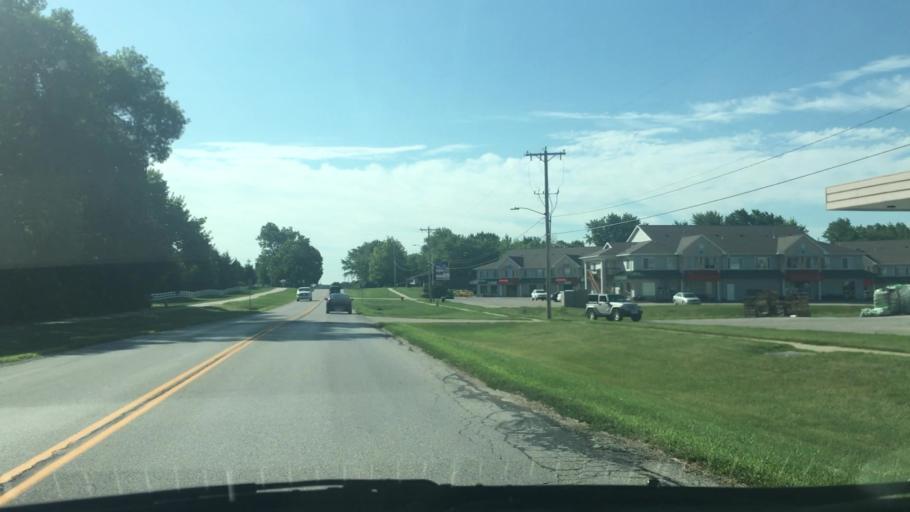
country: US
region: Iowa
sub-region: Johnson County
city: North Liberty
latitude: 41.7446
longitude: -91.5924
